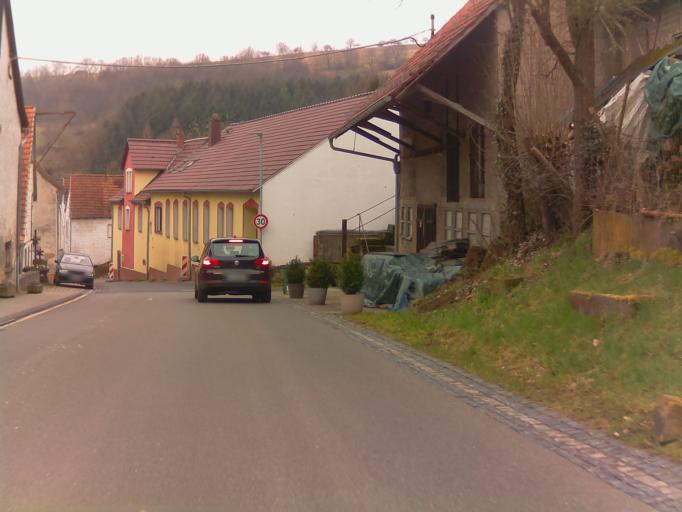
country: DE
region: Rheinland-Pfalz
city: Raumbach
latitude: 49.7234
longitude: 7.6484
